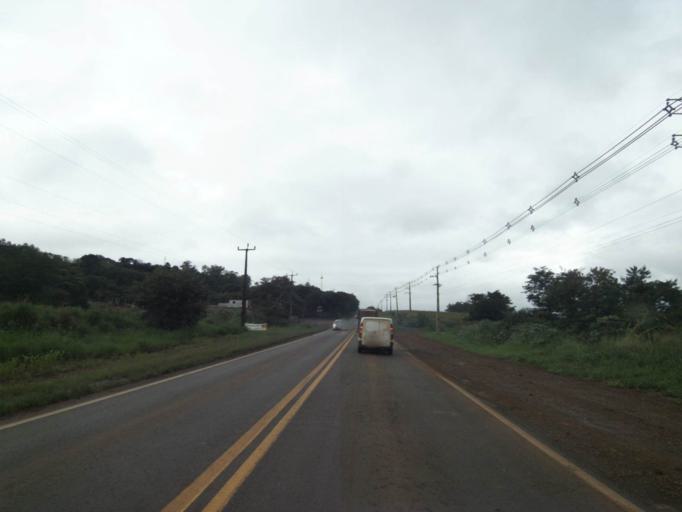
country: BR
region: Parana
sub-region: Marechal Candido Rondon
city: Marechal Candido Rondon
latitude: -24.5686
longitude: -54.0149
